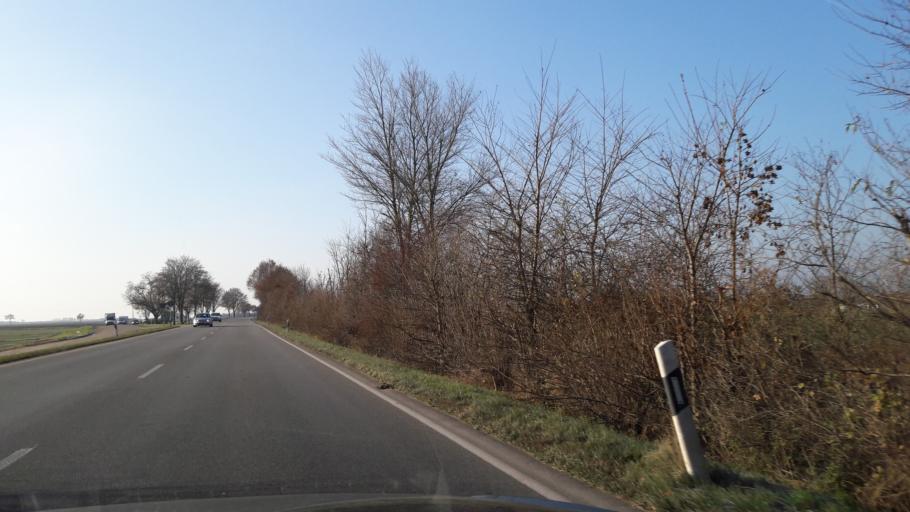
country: DE
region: Rheinland-Pfalz
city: Zeiskam
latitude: 49.2452
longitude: 8.2349
